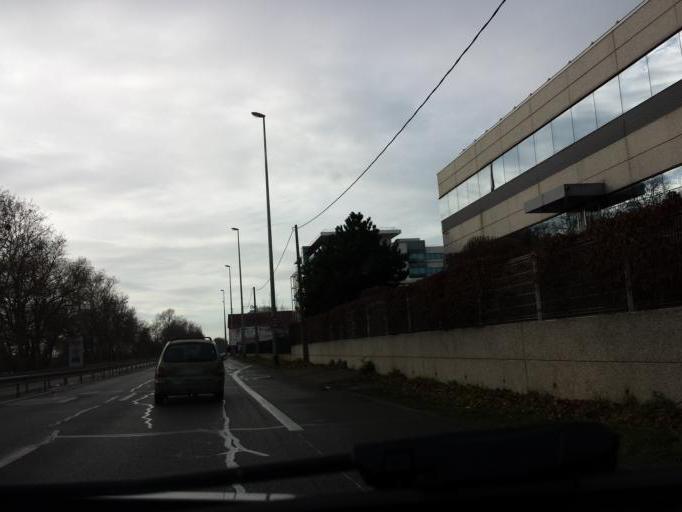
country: FR
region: Ile-de-France
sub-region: Departement du Val-d'Oise
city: Bezons
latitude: 48.9290
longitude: 2.2315
